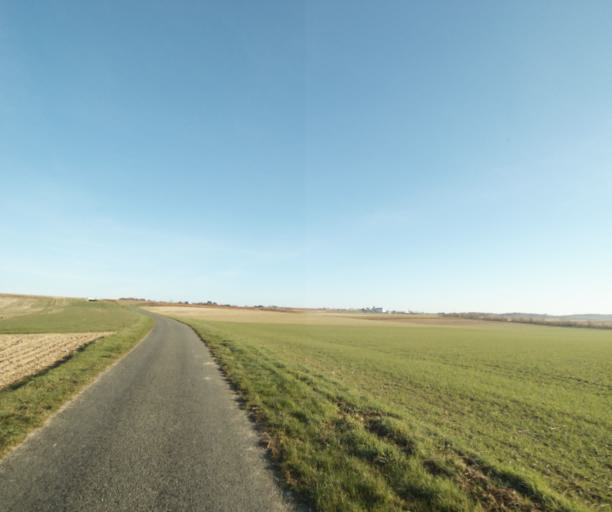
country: FR
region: Poitou-Charentes
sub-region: Departement de la Charente-Maritime
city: Cherac
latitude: 45.6959
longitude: -0.4564
